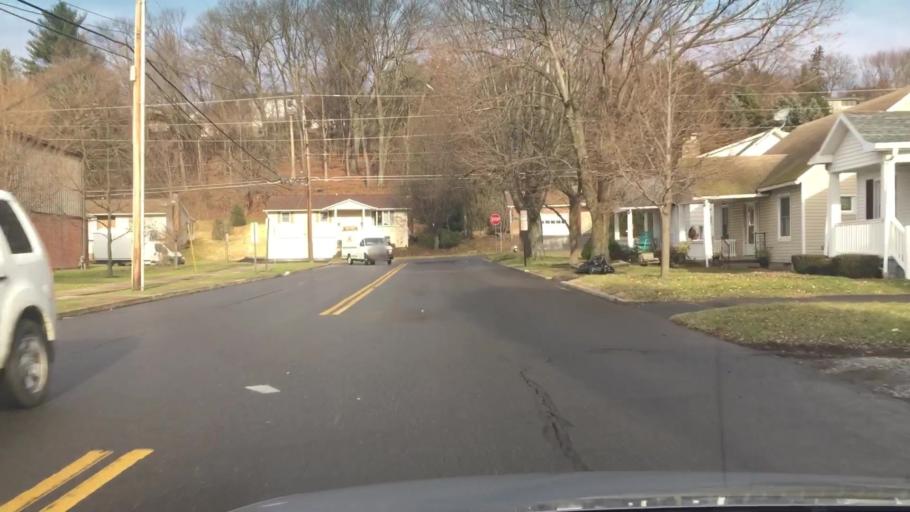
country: US
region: Pennsylvania
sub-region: Columbia County
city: Bloomsburg
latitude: 41.0043
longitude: -76.4425
